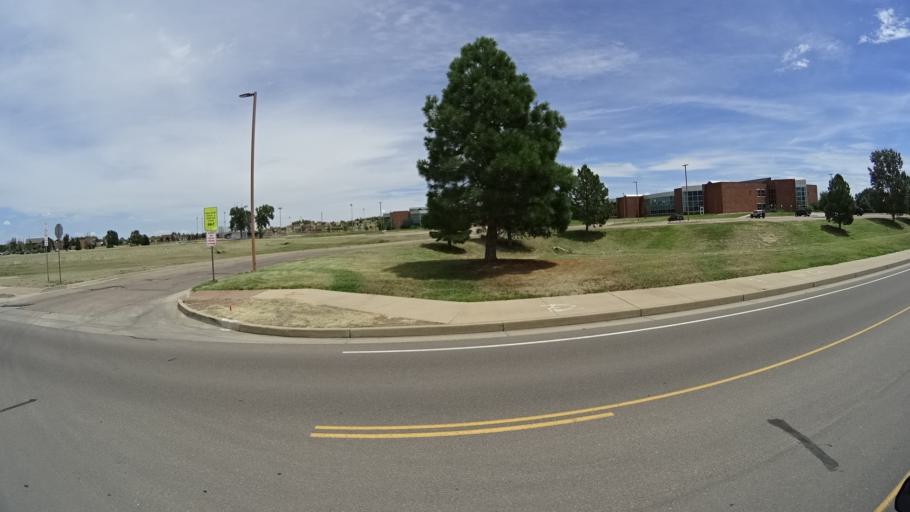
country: US
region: Colorado
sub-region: El Paso County
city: Fountain
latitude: 38.6728
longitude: -104.6859
